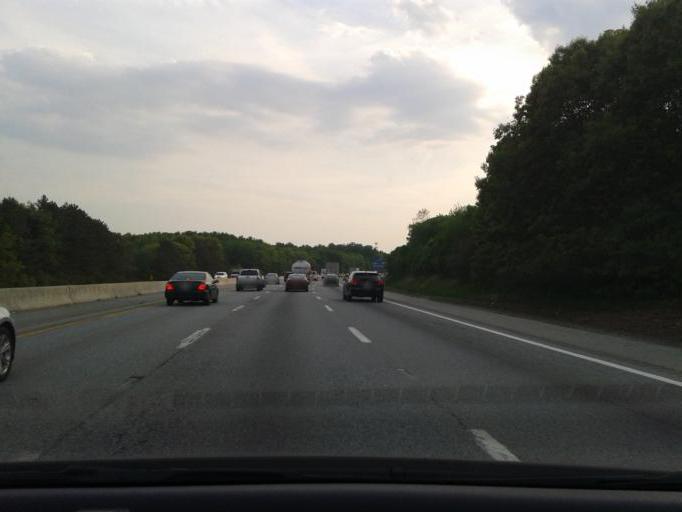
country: US
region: Massachusetts
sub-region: Middlesex County
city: Cochituate
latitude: 42.3197
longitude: -71.3433
